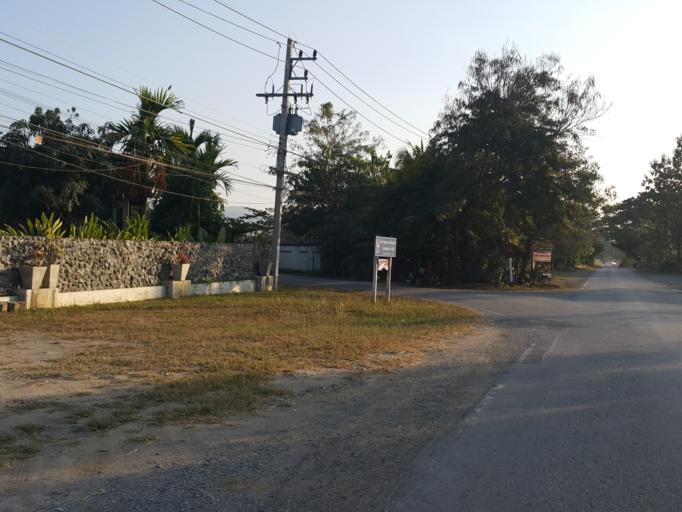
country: TH
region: Chiang Mai
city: Mae On
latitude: 18.7800
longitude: 99.2558
